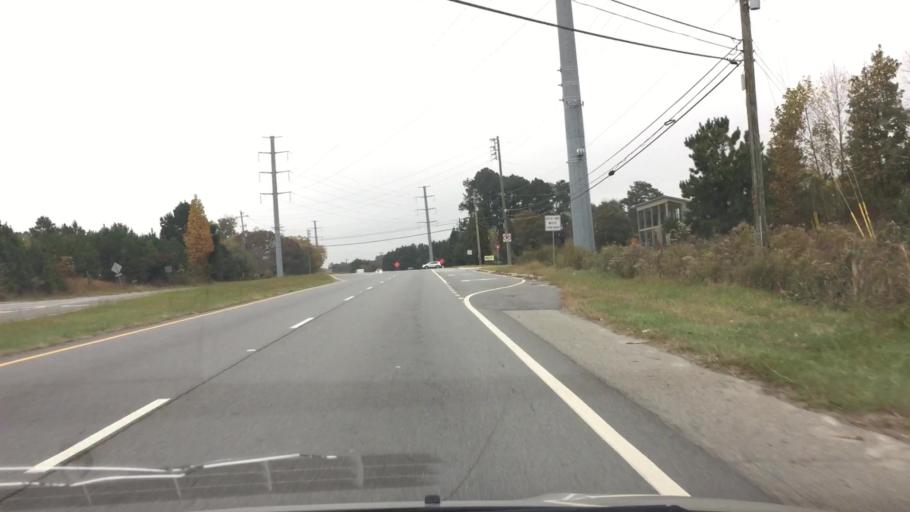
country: US
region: Georgia
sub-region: Fulton County
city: Milton
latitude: 34.1338
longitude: -84.2394
